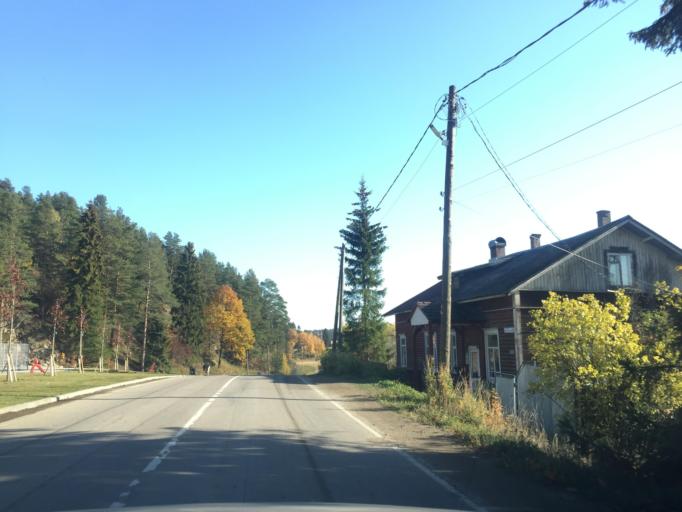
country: RU
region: Leningrad
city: Kuznechnoye
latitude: 61.2986
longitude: 29.9003
